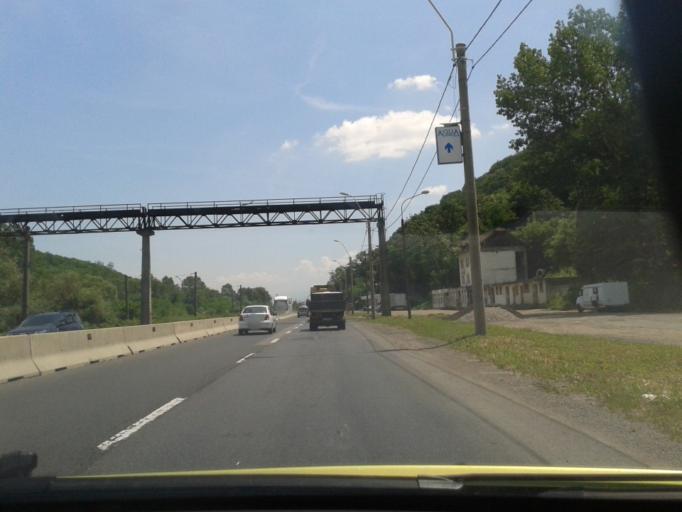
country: RO
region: Hunedoara
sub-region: Comuna Soimus
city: Soimus
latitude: 45.9047
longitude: 22.8799
